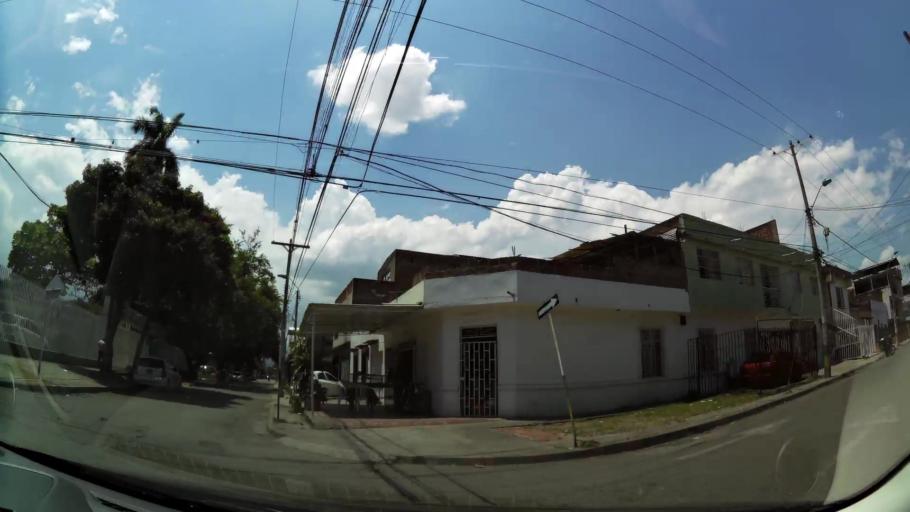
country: CO
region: Valle del Cauca
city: Cali
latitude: 3.4465
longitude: -76.5000
